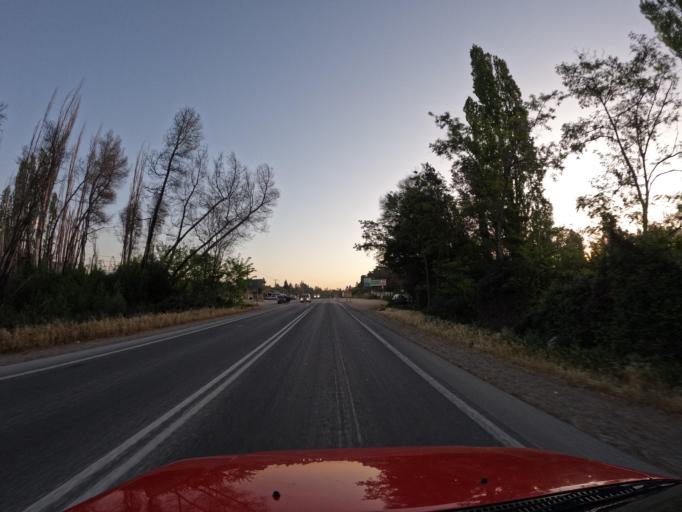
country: CL
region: O'Higgins
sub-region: Provincia de Cachapoal
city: San Vicente
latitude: -34.1645
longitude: -71.3947
